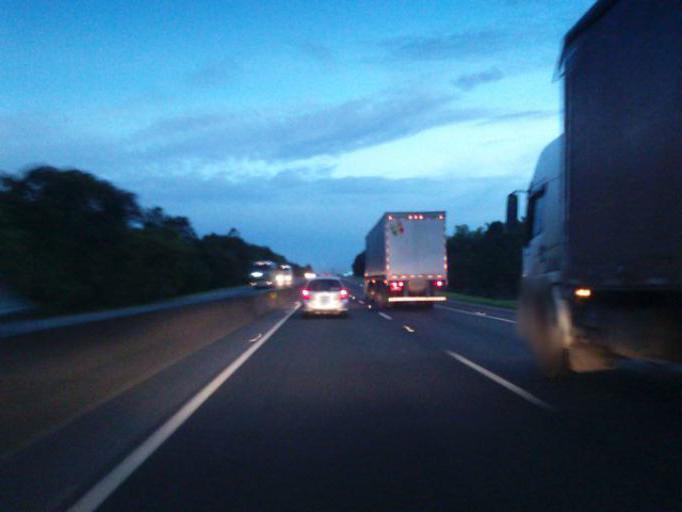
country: BR
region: Santa Catarina
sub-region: Barra Velha
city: Barra Velha
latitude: -26.5009
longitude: -48.7294
